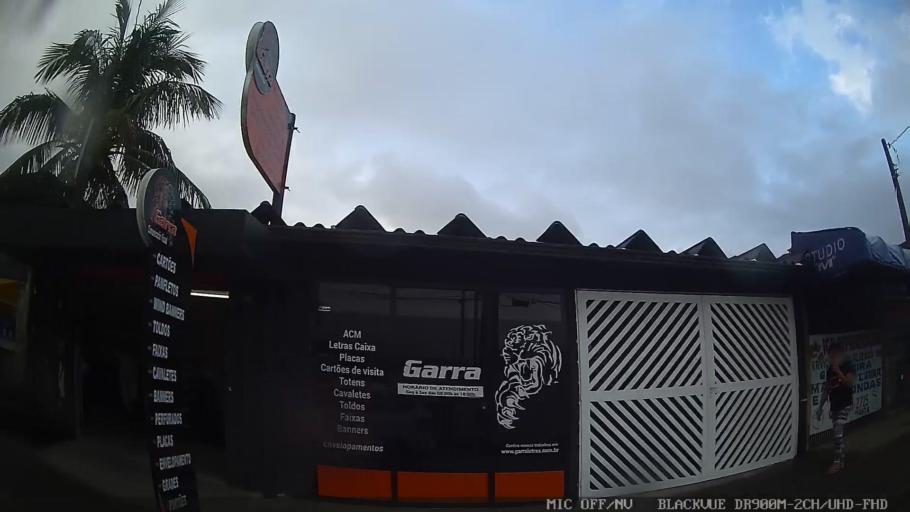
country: BR
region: Sao Paulo
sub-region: Itanhaem
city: Itanhaem
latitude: -24.1691
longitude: -46.7836
